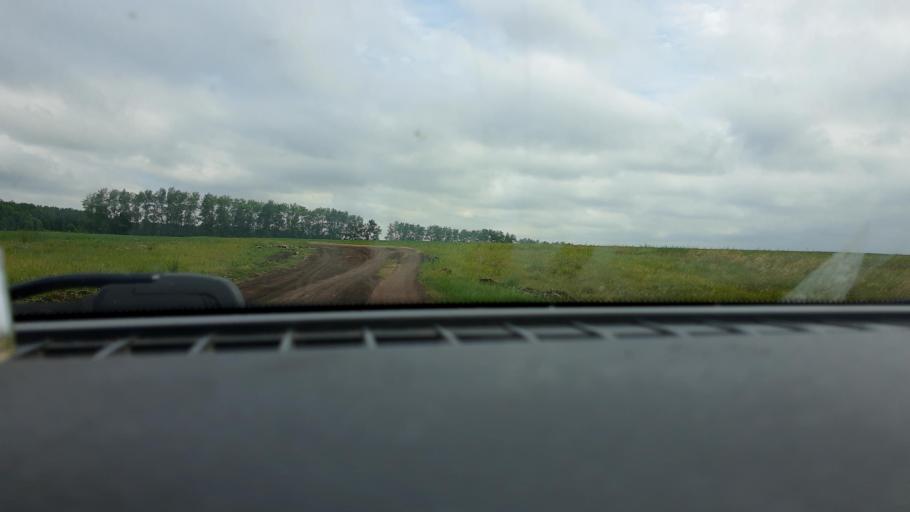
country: RU
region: Bashkortostan
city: Chishmy
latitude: 54.6933
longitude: 55.4873
